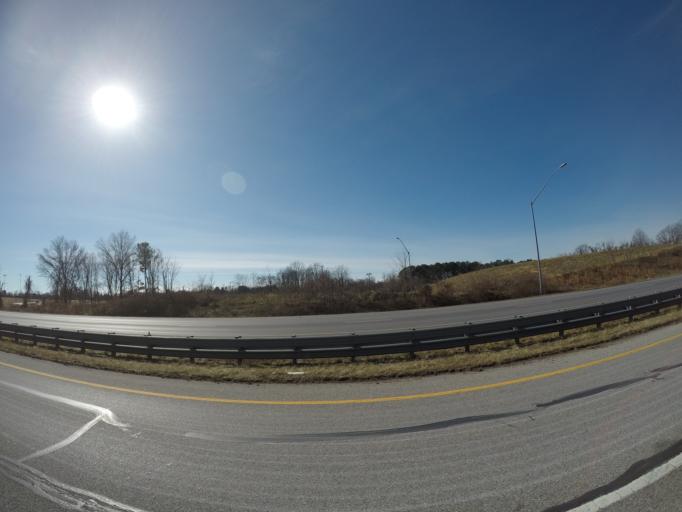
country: US
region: Maryland
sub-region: Howard County
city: Columbia
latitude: 39.2136
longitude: -76.8337
